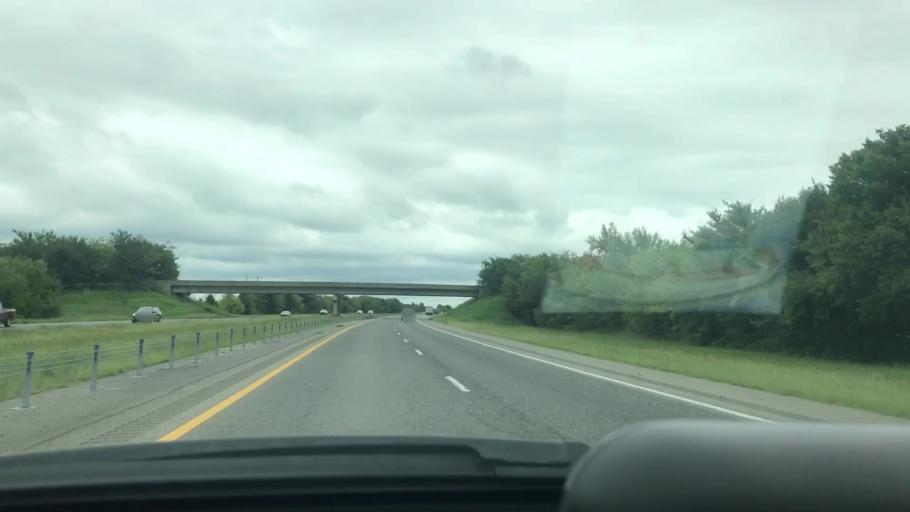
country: US
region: Oklahoma
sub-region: McIntosh County
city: Checotah
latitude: 35.4333
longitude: -95.5553
